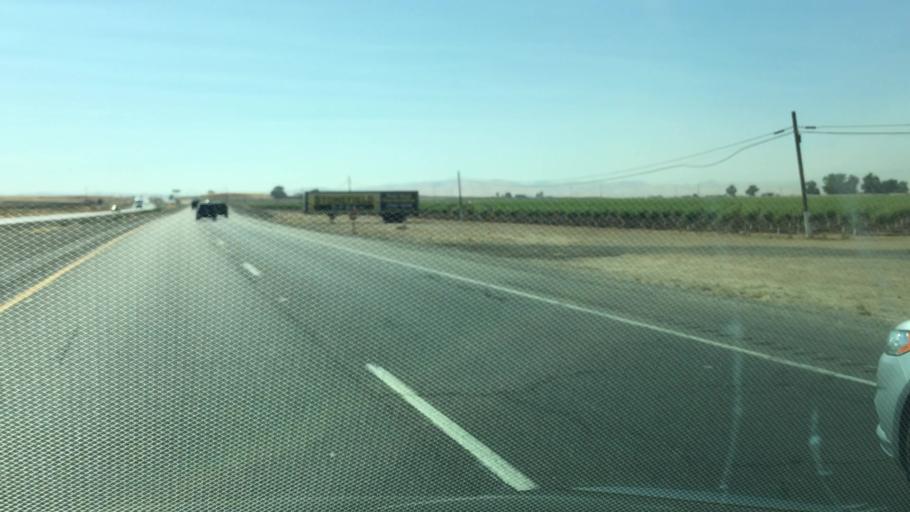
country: US
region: California
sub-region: Merced County
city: Los Banos
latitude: 37.0566
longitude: -120.9360
